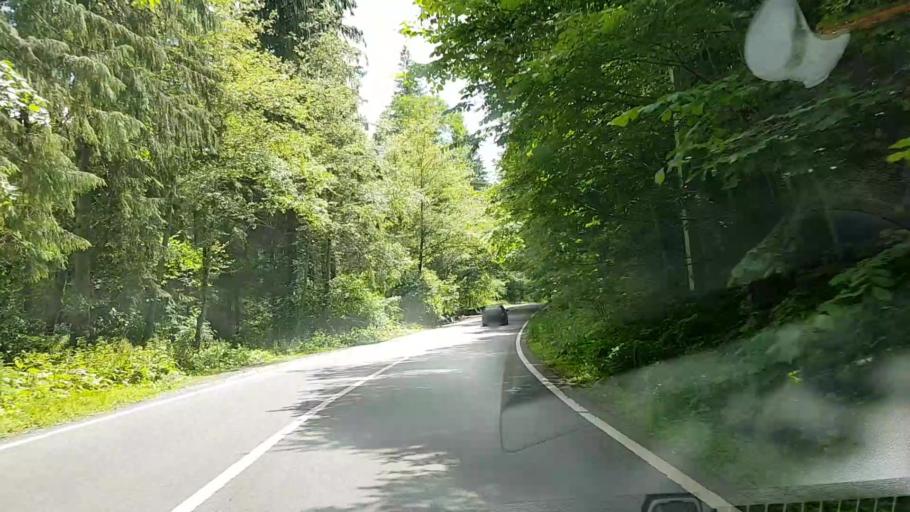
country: RO
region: Suceava
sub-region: Comuna Crucea
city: Crucea
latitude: 47.3067
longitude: 25.6264
